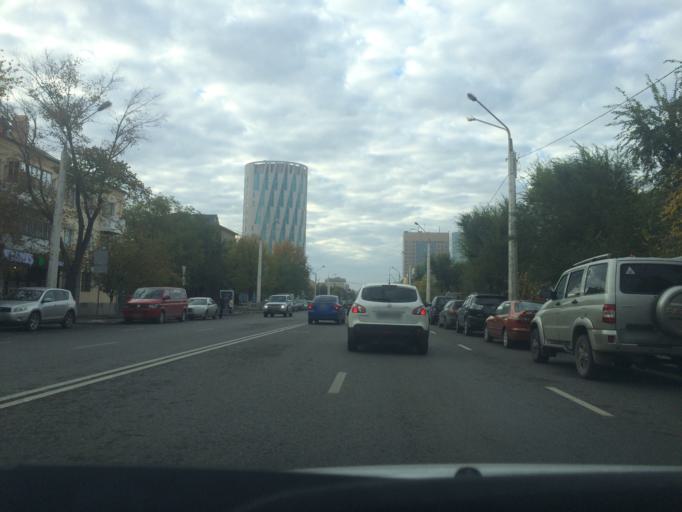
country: KZ
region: Astana Qalasy
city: Astana
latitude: 51.1729
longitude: 71.4194
